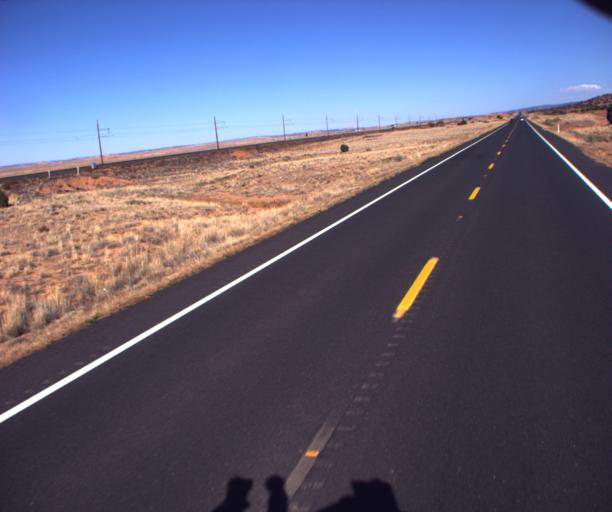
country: US
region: Arizona
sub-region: Coconino County
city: Kaibito
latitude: 36.4144
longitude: -110.8177
